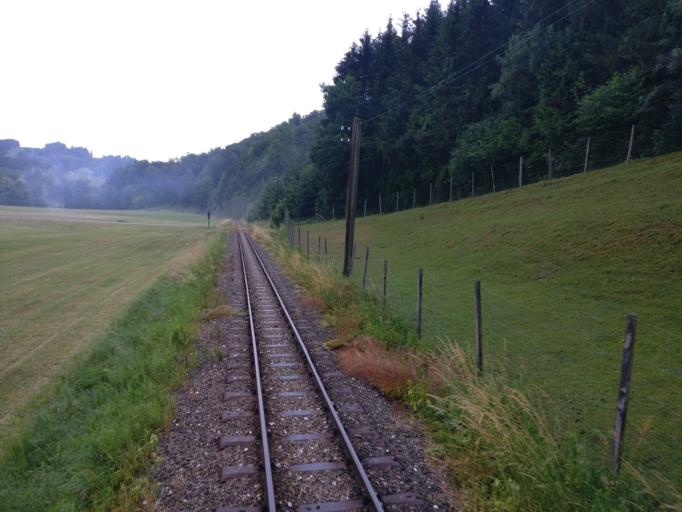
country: AT
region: Upper Austria
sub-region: Politischer Bezirk Kirchdorf an der Krems
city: Gruenburg
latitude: 47.9887
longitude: 14.2801
